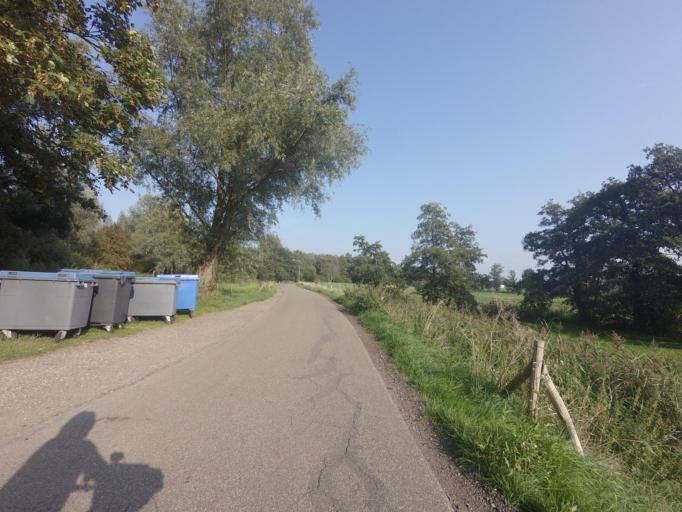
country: NL
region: Groningen
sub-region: Gemeente Haren
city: Haren
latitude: 53.1731
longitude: 6.5815
